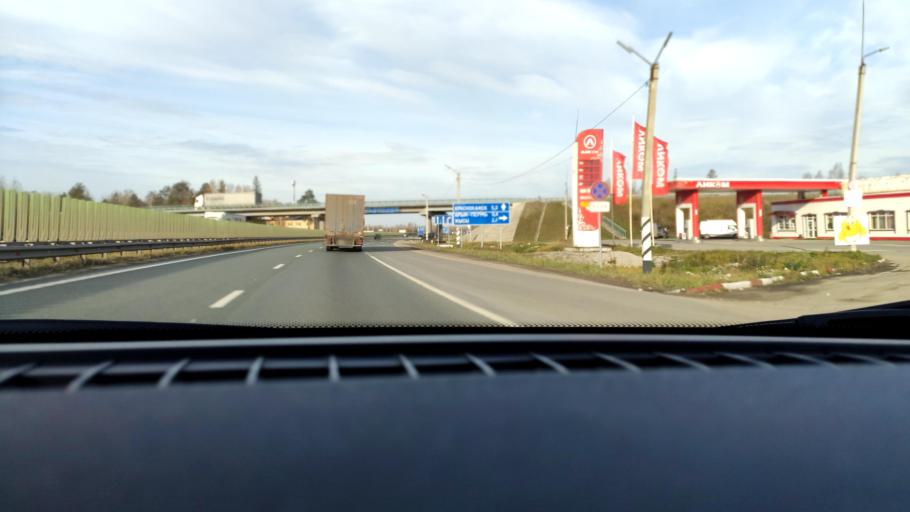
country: RU
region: Perm
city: Overyata
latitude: 58.0428
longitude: 55.8771
